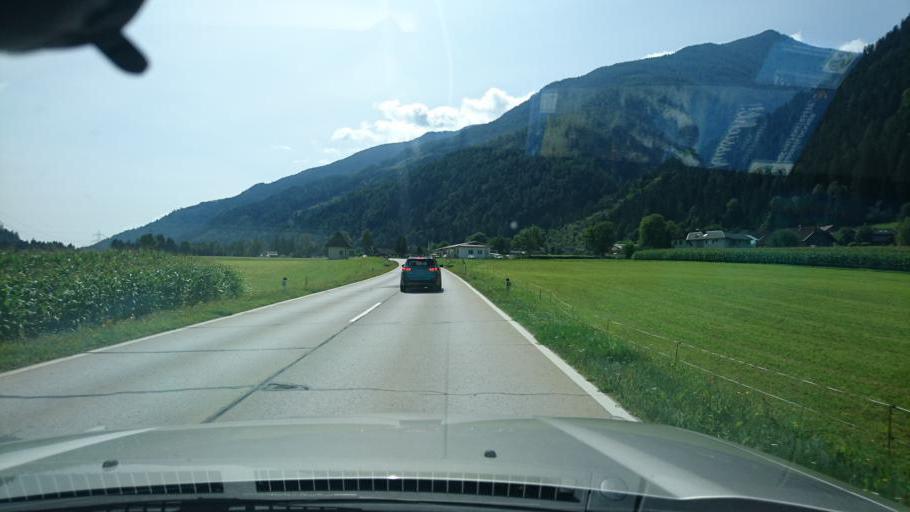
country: AT
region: Carinthia
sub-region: Politischer Bezirk Spittal an der Drau
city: Obervellach
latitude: 46.8914
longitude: 13.2634
